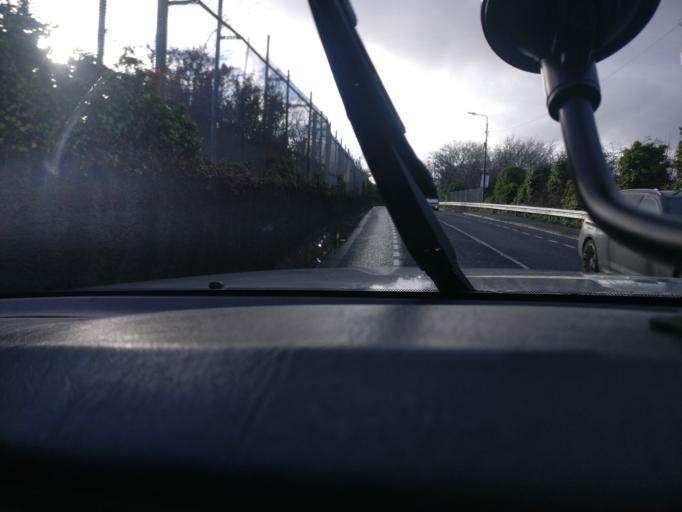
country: IE
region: Leinster
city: Crumlin
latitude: 53.3150
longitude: -6.3371
